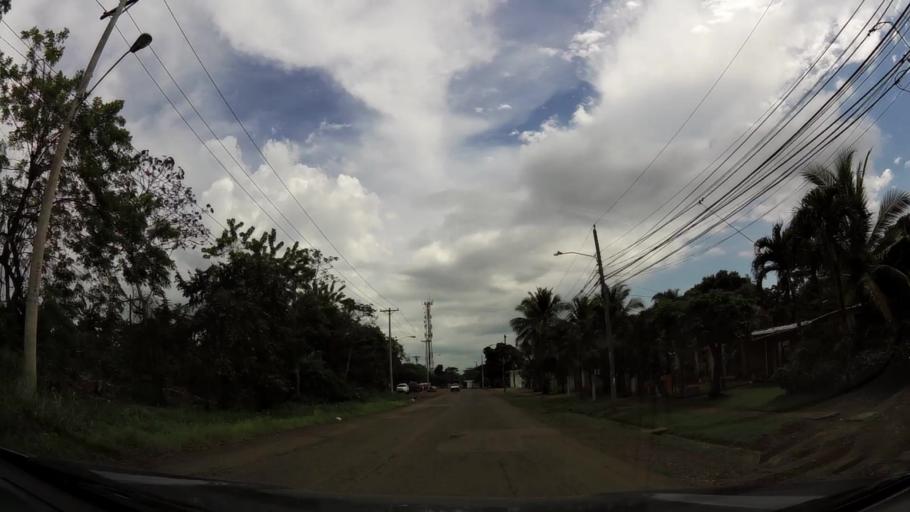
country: PA
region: Panama
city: Cabra Numero Uno
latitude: 9.1125
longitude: -79.3306
